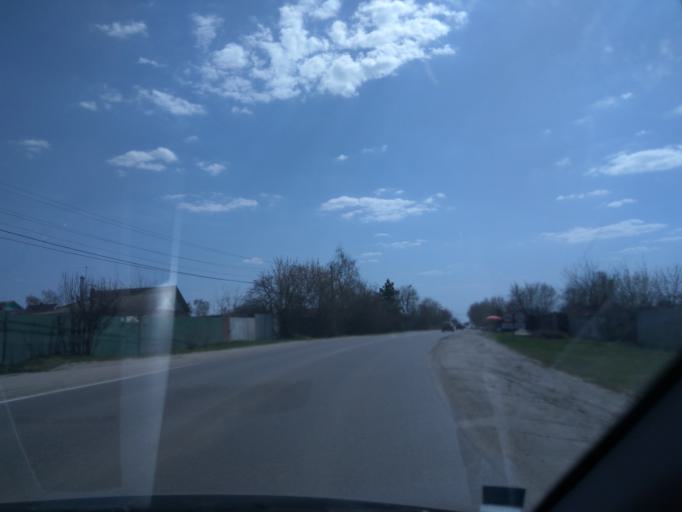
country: RU
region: Moskovskaya
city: Ramenskoye
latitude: 55.5569
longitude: 38.2314
